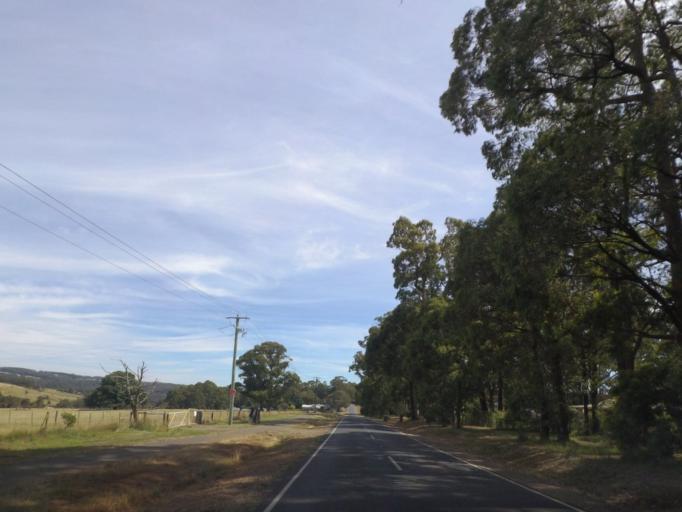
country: AU
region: Victoria
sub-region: Nillumbik
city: Saint Andrews
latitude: -37.5170
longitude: 145.3541
